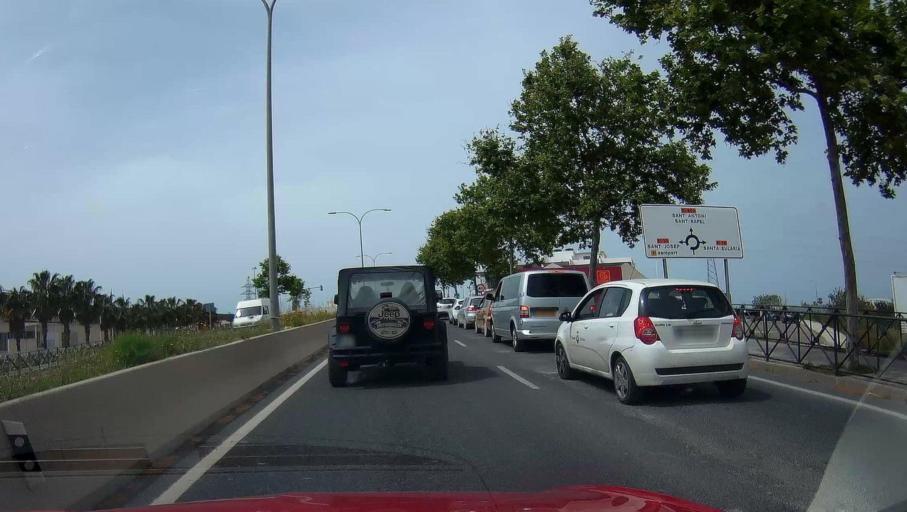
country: ES
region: Balearic Islands
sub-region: Illes Balears
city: Ibiza
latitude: 38.9190
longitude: 1.4264
